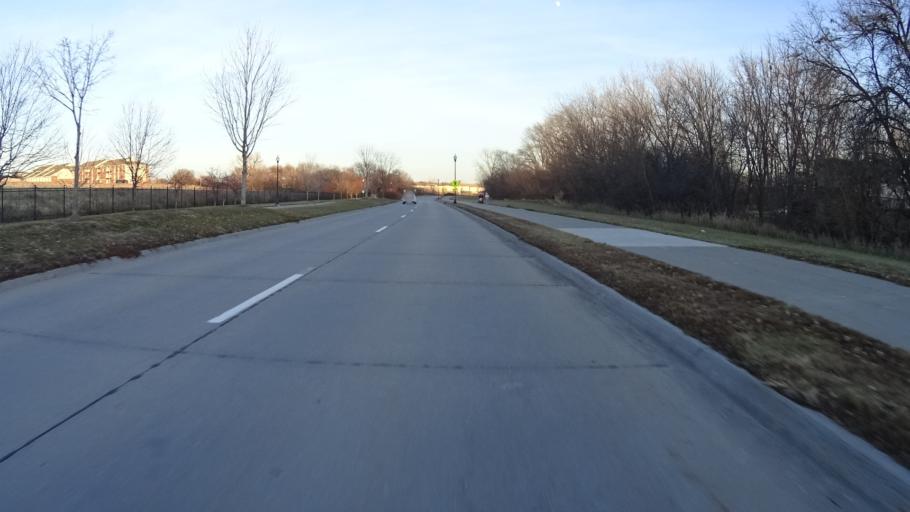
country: US
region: Nebraska
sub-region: Sarpy County
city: Papillion
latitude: 41.1328
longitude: -96.0386
